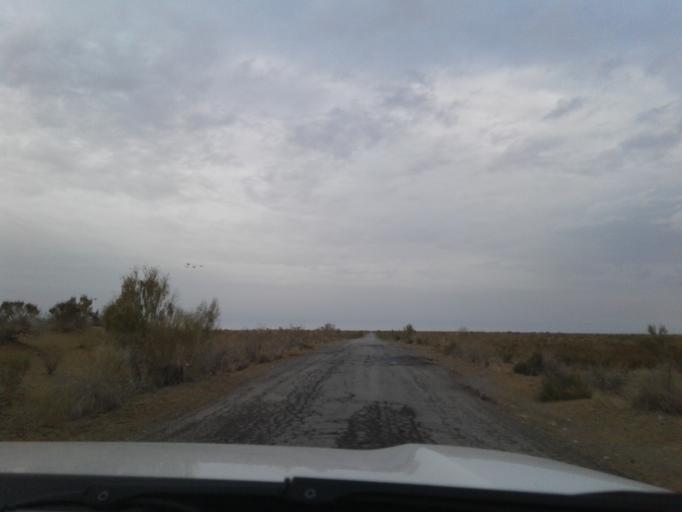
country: TM
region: Mary
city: Mary
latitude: 38.4645
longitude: 61.6700
